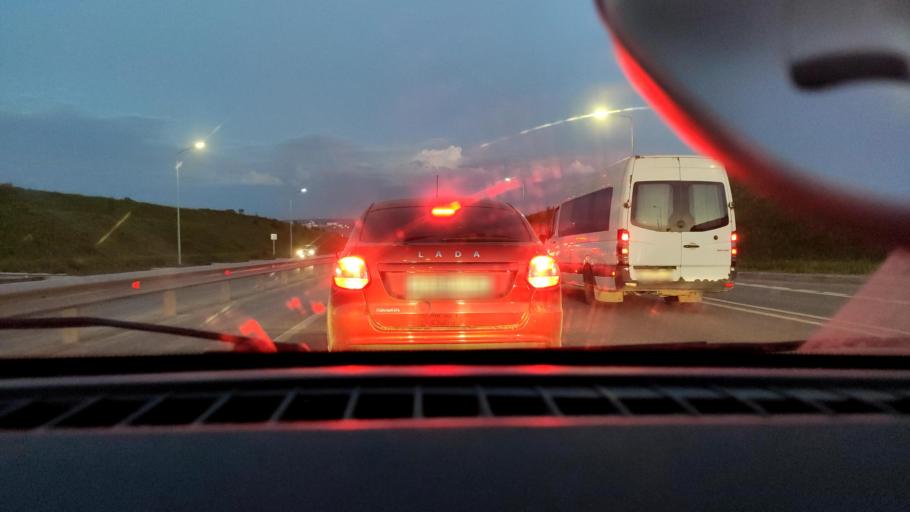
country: RU
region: Perm
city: Polazna
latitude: 58.1958
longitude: 56.4055
